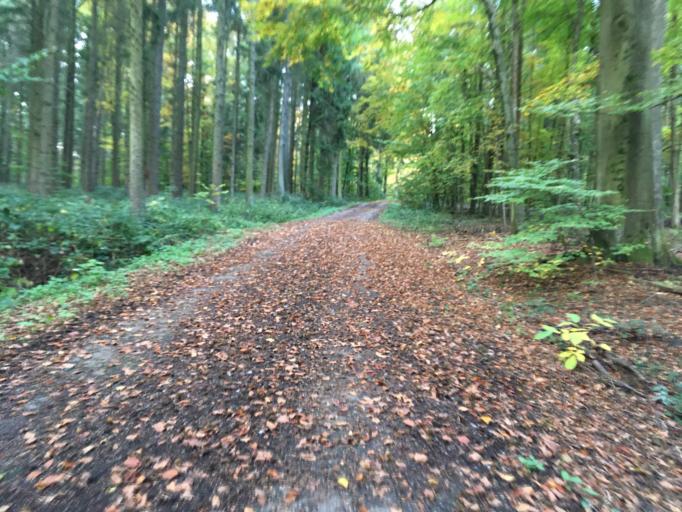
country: DE
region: Baden-Wuerttemberg
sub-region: Regierungsbezirk Stuttgart
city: Ittlingen
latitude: 49.2384
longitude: 8.9502
